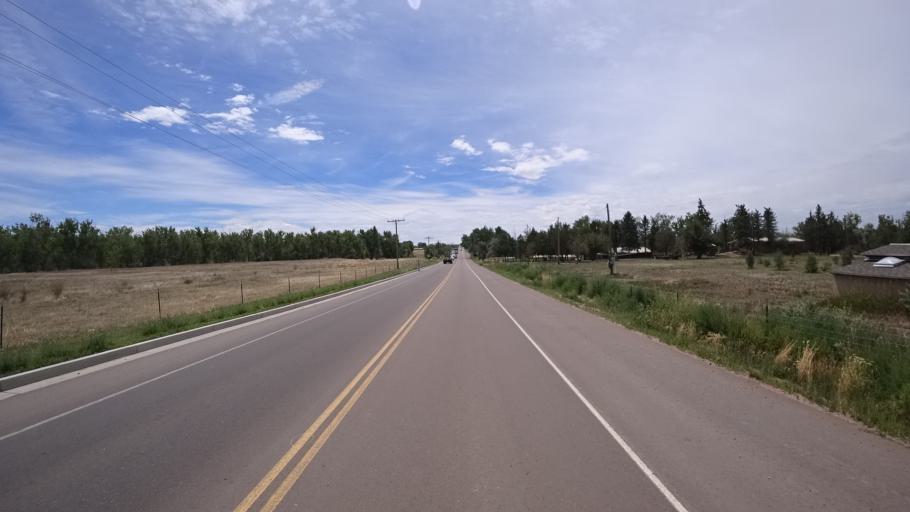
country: US
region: Colorado
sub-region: El Paso County
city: Fountain
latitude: 38.7036
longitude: -104.6736
